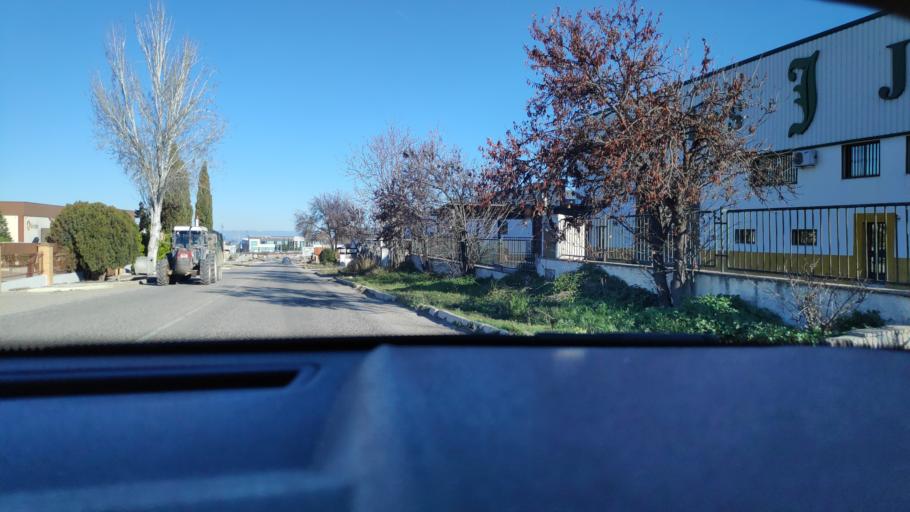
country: ES
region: Andalusia
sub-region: Provincia de Jaen
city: Mancha Real
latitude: 37.8038
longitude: -3.6110
